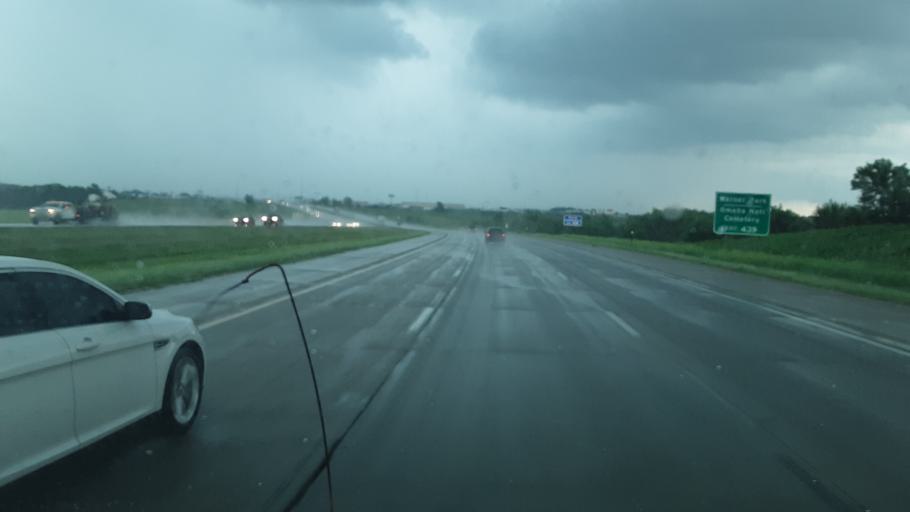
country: US
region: Nebraska
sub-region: Sarpy County
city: Chalco
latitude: 41.1344
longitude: -96.1715
